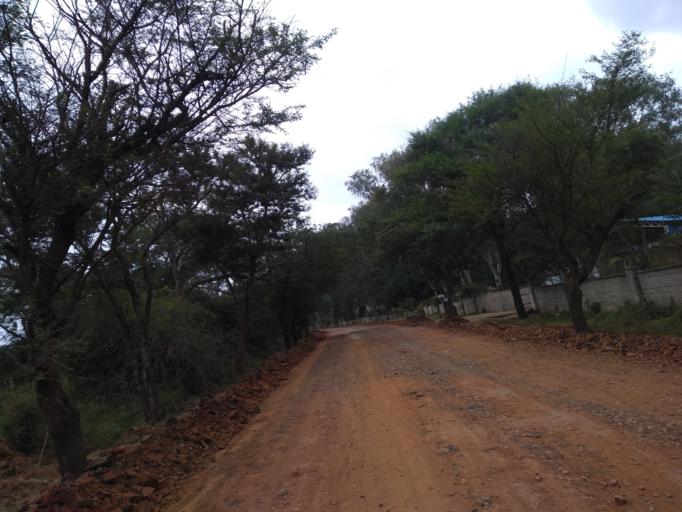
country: IN
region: Karnataka
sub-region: Bangalore Rural
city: Nelamangala
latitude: 13.1522
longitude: 77.4741
